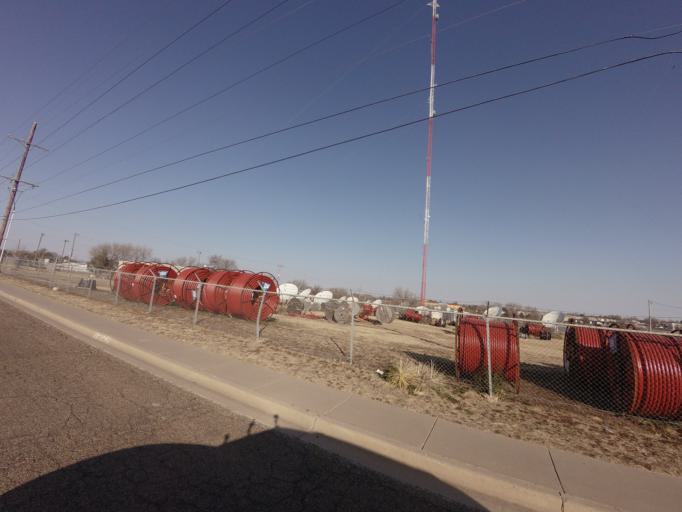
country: US
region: New Mexico
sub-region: Curry County
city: Clovis
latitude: 34.4157
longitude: -103.2077
